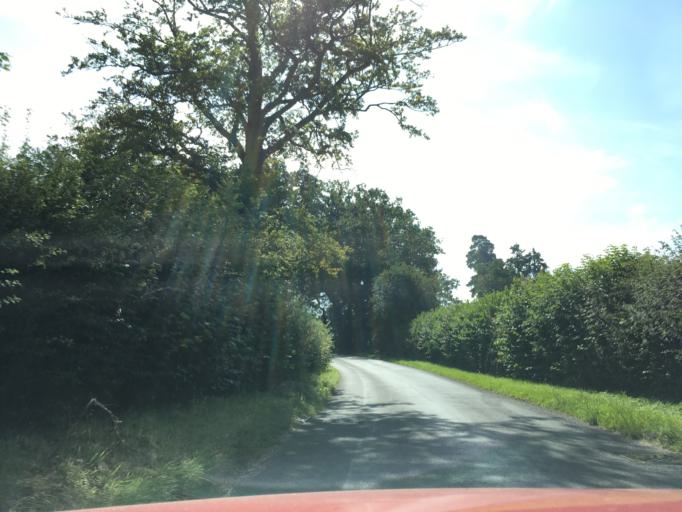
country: GB
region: England
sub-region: Hampshire
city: Highclere
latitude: 51.3609
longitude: -1.3934
